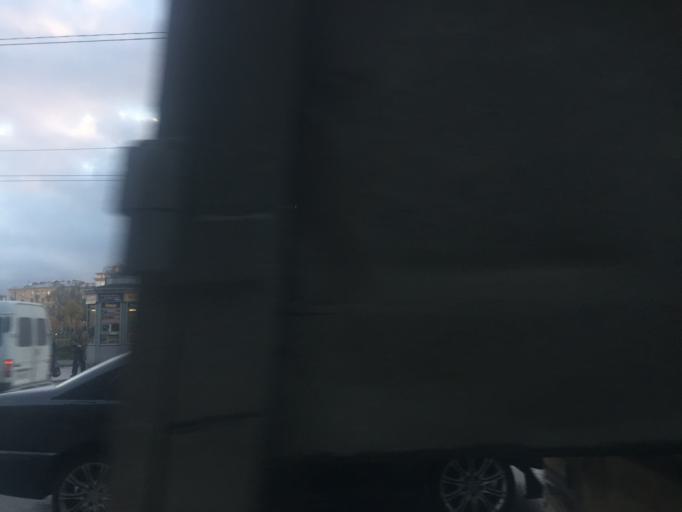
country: RU
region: St.-Petersburg
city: Obukhovo
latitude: 59.8785
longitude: 30.4412
